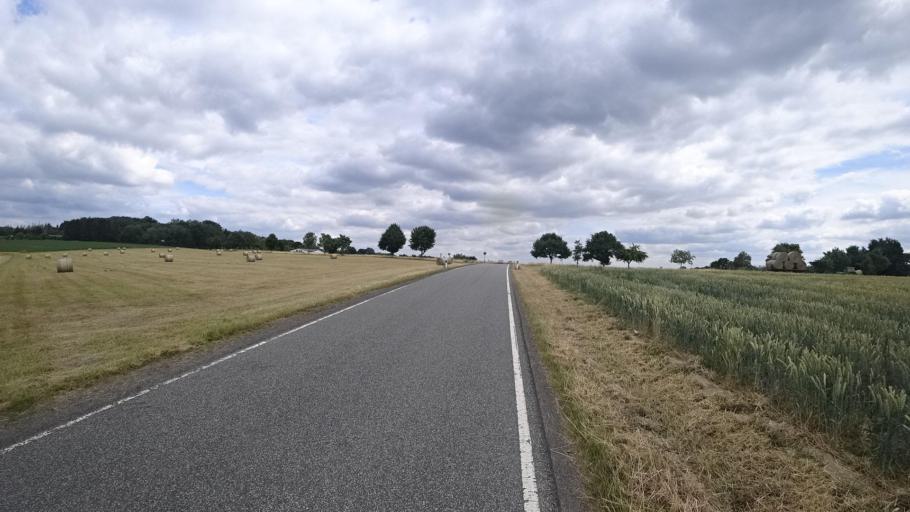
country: DE
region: Rheinland-Pfalz
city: Wolmersen
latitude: 50.7173
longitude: 7.5922
